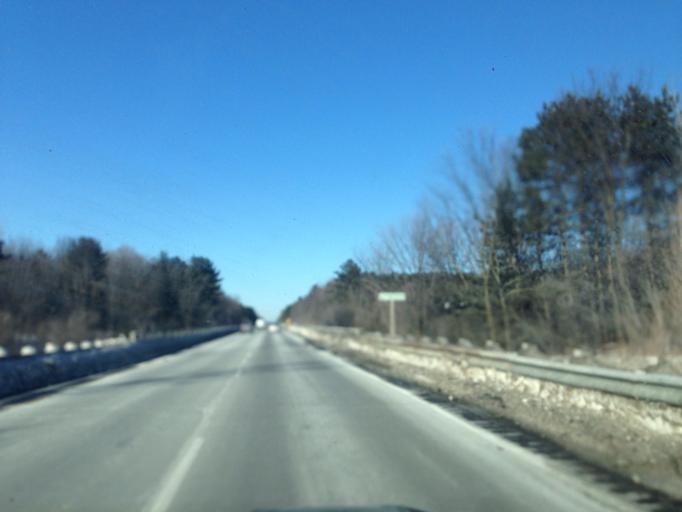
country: CA
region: Ontario
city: Ottawa
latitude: 45.3628
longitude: -75.4846
